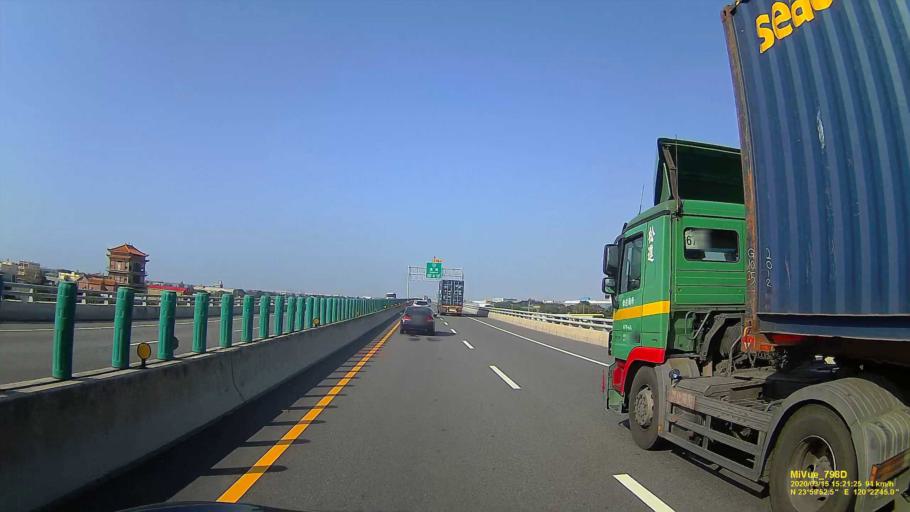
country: TW
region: Taiwan
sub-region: Changhua
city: Chang-hua
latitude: 23.9984
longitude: 120.3793
